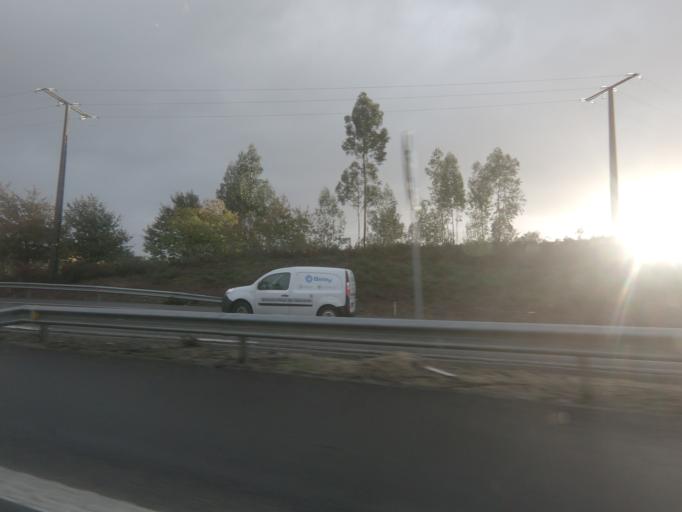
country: ES
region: Galicia
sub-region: Provincia de Pontevedra
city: Redondela
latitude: 42.2252
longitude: -8.6440
